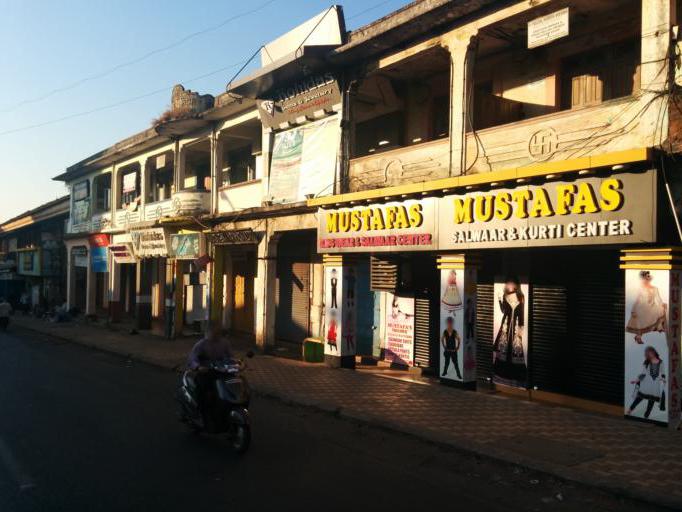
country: IN
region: Goa
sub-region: South Goa
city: Madgaon
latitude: 15.2714
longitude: 73.9588
